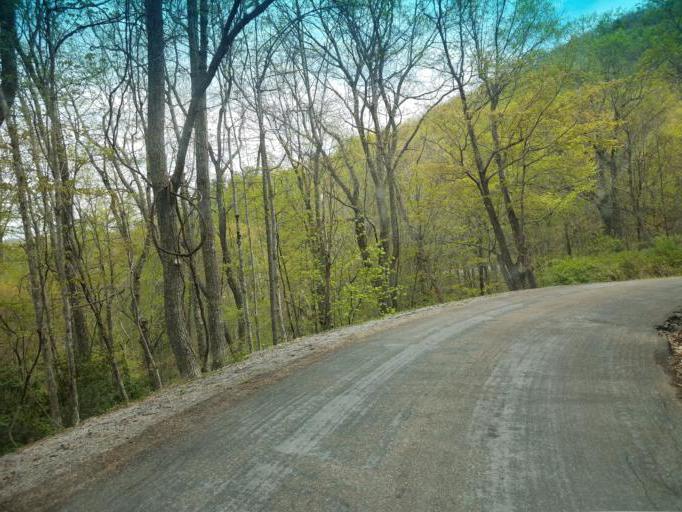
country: US
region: Virginia
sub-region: Smyth County
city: Marion
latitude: 36.7964
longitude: -81.4652
